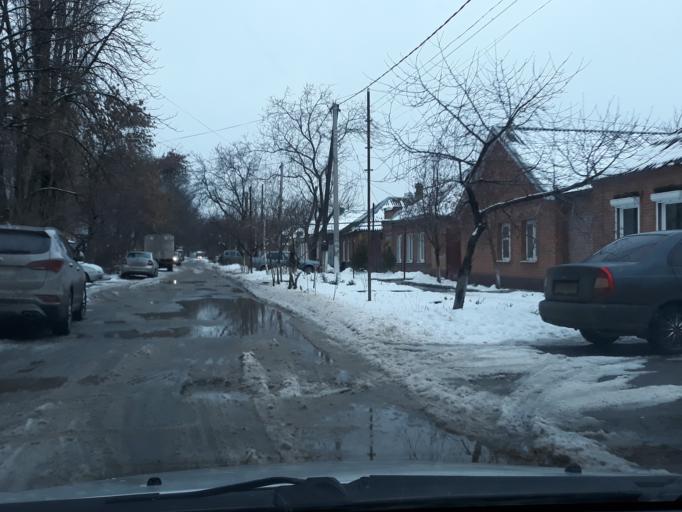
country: RU
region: Rostov
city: Taganrog
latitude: 47.2402
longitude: 38.8796
